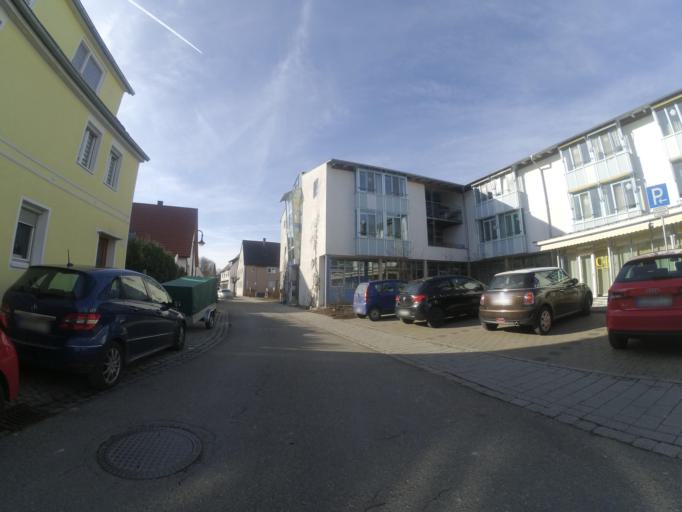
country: DE
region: Baden-Wuerttemberg
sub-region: Regierungsbezirk Stuttgart
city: Herbrechtingen
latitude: 48.6235
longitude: 10.1746
